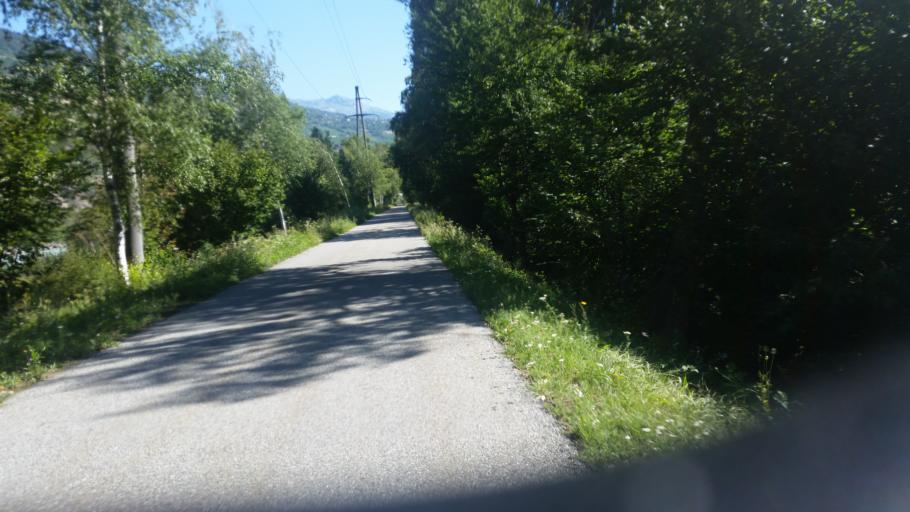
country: CH
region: Valais
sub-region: Sierre District
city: Grone
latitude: 46.2588
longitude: 7.4493
